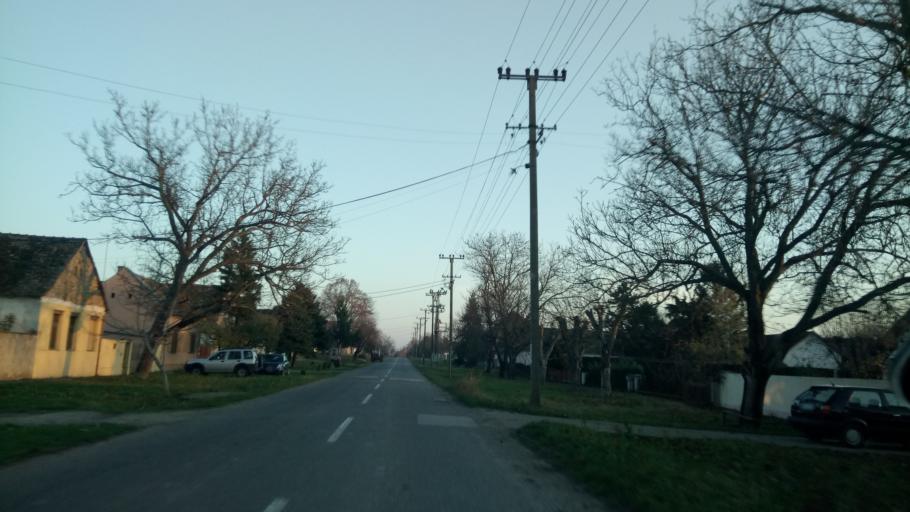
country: RS
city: Surduk
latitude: 45.0822
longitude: 20.3094
